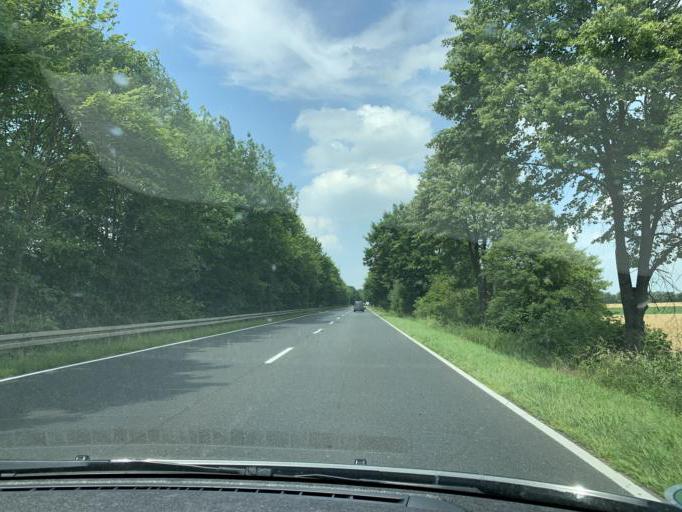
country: DE
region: North Rhine-Westphalia
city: Siersdorf
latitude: 50.8584
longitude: 6.2293
